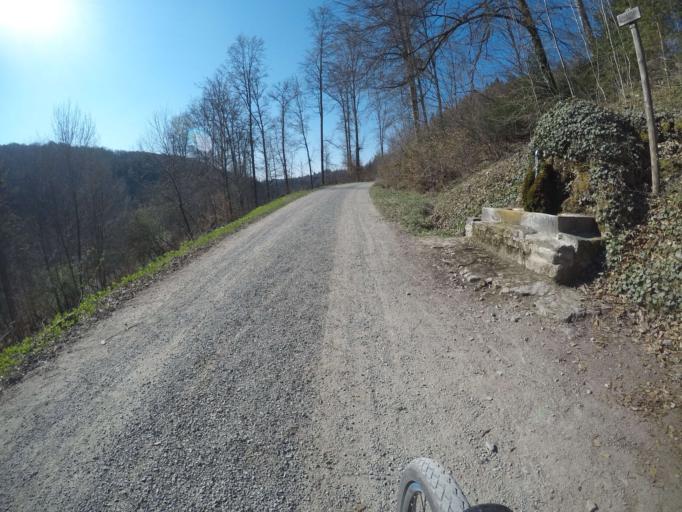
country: DE
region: Baden-Wuerttemberg
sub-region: Tuebingen Region
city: Tuebingen
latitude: 48.5726
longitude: 9.0323
